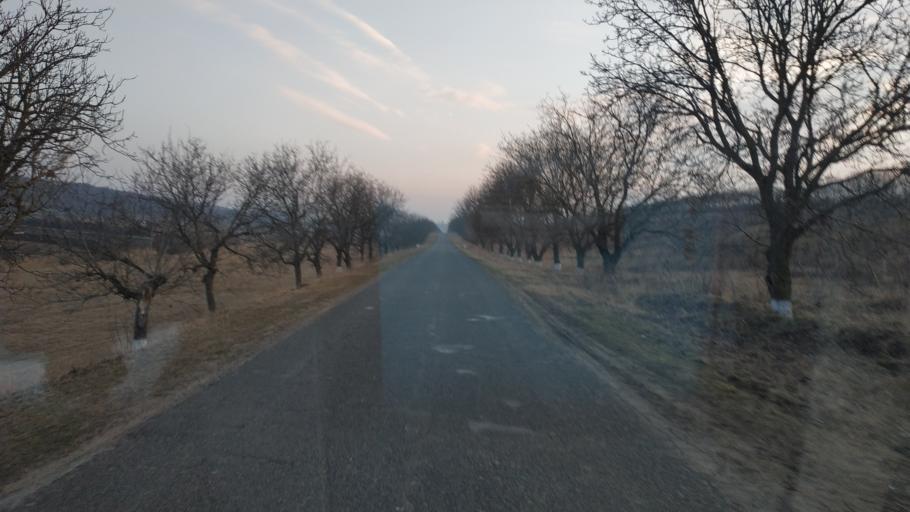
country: MD
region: Hincesti
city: Dancu
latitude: 46.6893
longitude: 28.3359
